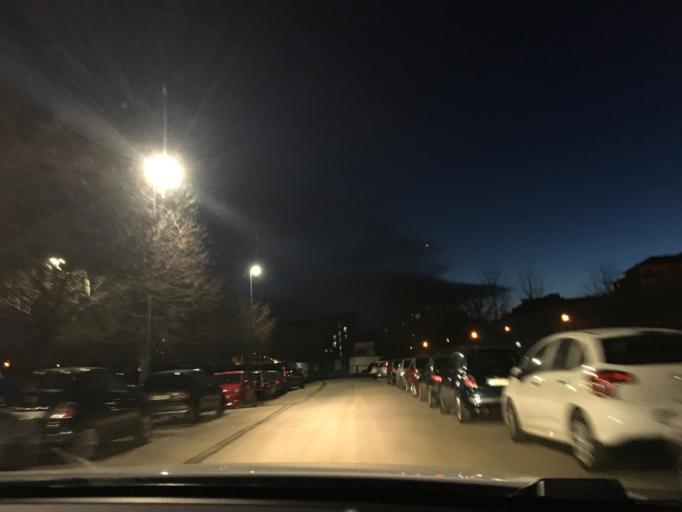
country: IT
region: Piedmont
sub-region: Provincia di Torino
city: Lesna
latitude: 45.0523
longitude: 7.6449
